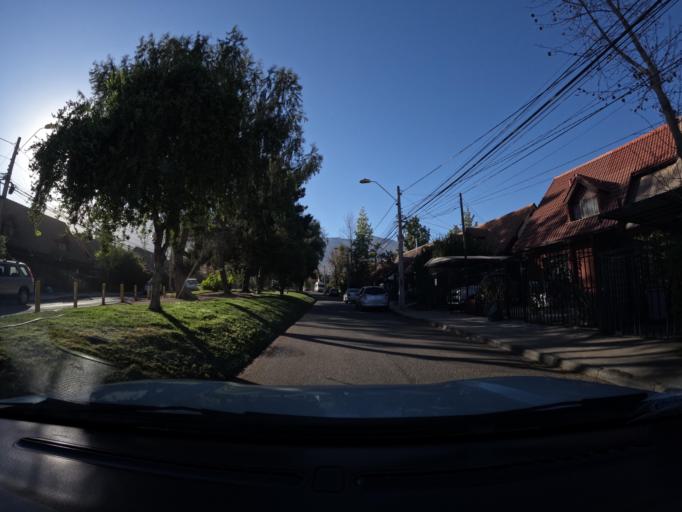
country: CL
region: Santiago Metropolitan
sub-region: Provincia de Santiago
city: Villa Presidente Frei, Nunoa, Santiago, Chile
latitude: -33.4801
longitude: -70.5485
